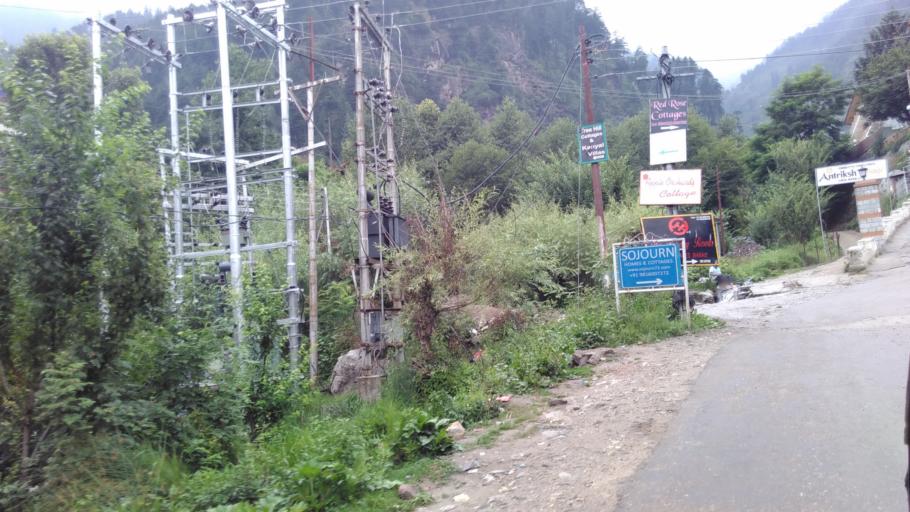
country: IN
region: Himachal Pradesh
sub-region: Kulu
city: Manali
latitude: 32.2195
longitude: 77.1863
